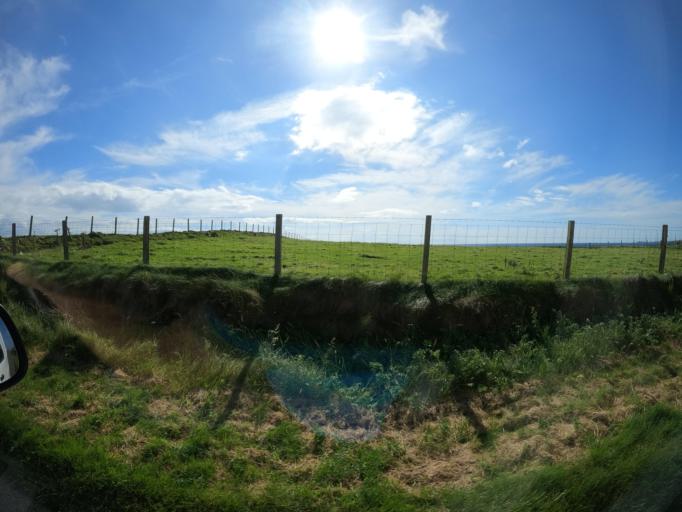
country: GB
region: Scotland
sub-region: Eilean Siar
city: Barra
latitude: 56.4929
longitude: -6.8226
